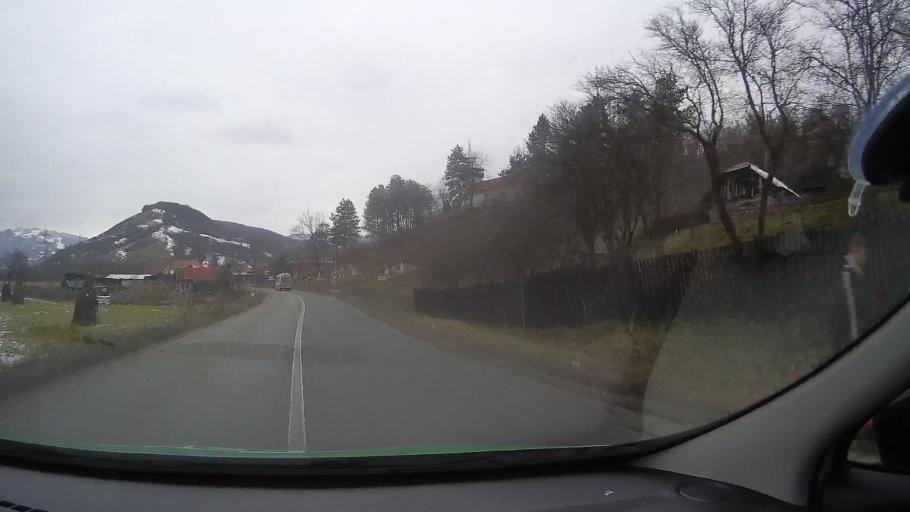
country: RO
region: Alba
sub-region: Comuna Metes
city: Metes
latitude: 46.0970
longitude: 23.4218
